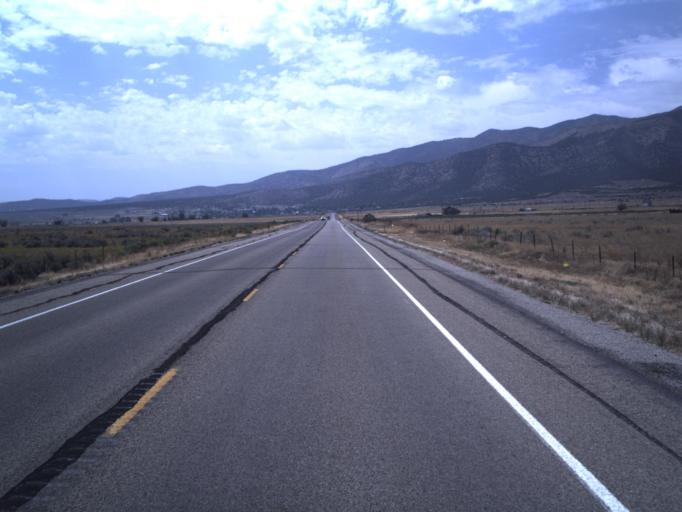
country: US
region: Utah
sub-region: Utah County
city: Eagle Mountain
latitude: 40.3523
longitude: -112.0694
